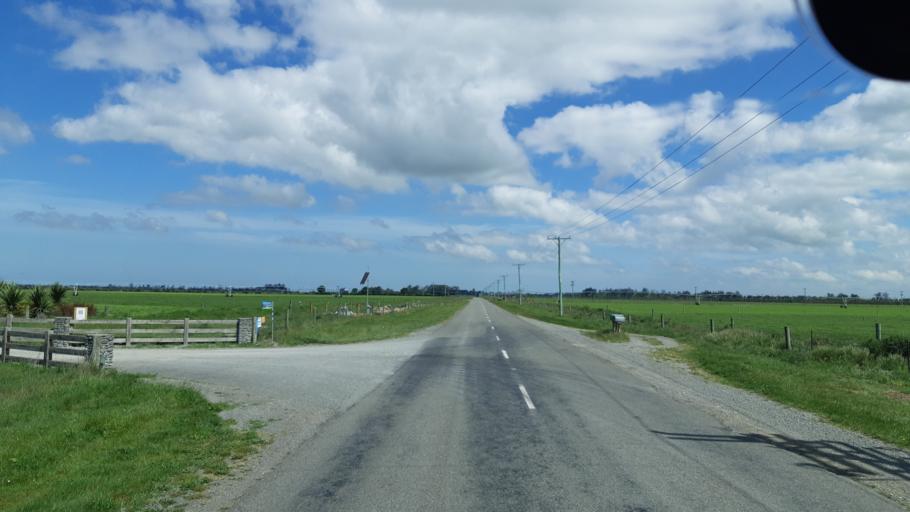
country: NZ
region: Canterbury
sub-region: Ashburton District
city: Tinwald
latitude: -44.0140
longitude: 171.4269
